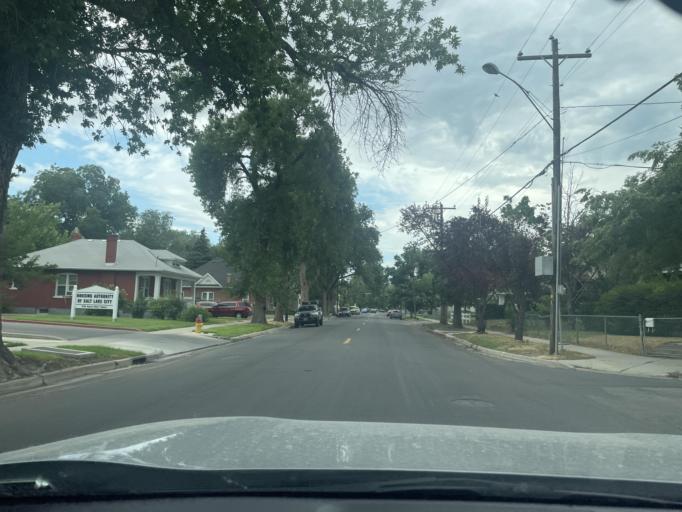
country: US
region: Utah
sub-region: Salt Lake County
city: South Salt Lake
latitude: 40.7317
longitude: -111.8940
